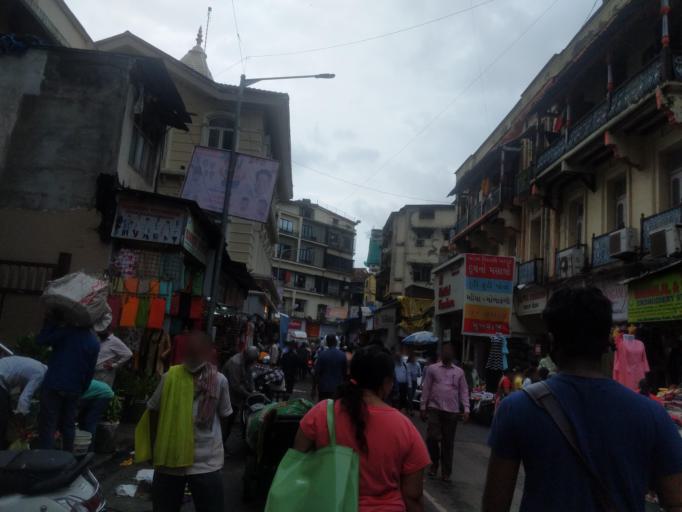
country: IN
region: Maharashtra
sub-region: Mumbai Suburban
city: Mumbai
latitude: 18.9534
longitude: 72.8275
